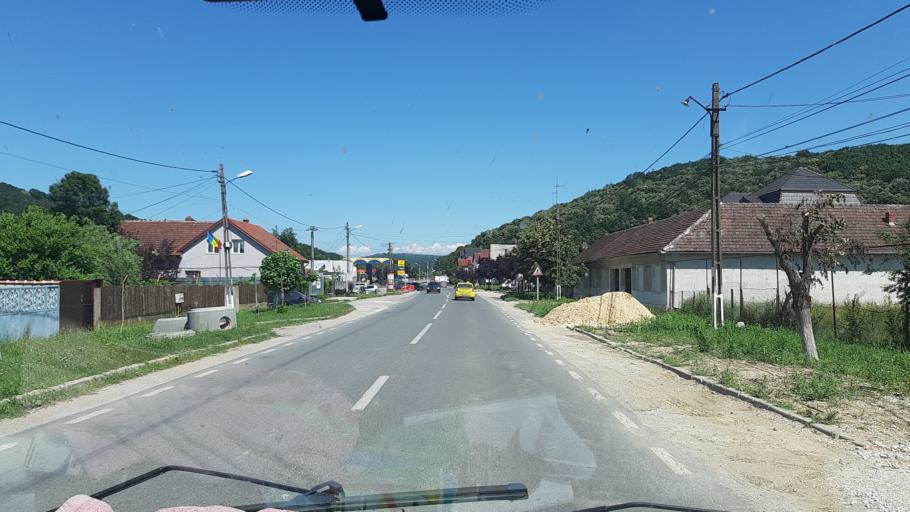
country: RO
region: Caras-Severin
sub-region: Oras Bocsa
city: Bocsa
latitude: 45.3801
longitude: 21.7370
